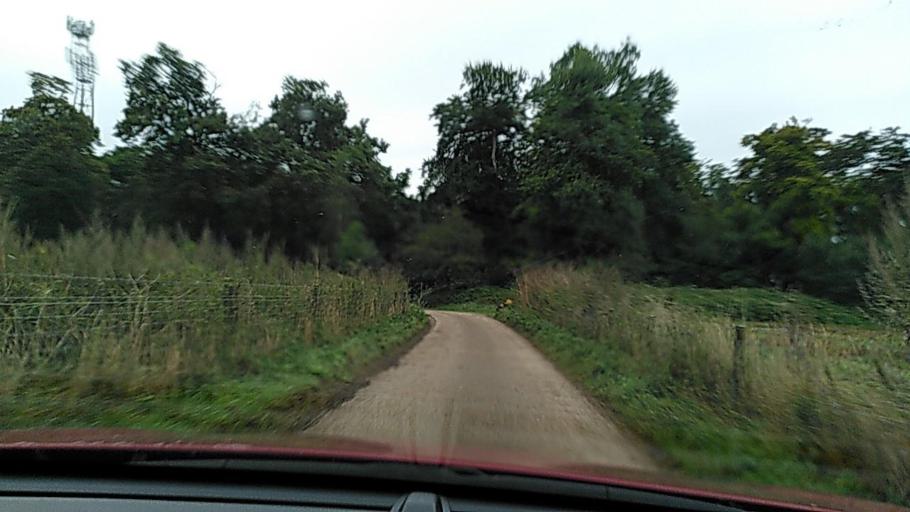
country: GB
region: England
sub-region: West Berkshire
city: Tilehurst
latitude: 51.4840
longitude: -1.0199
